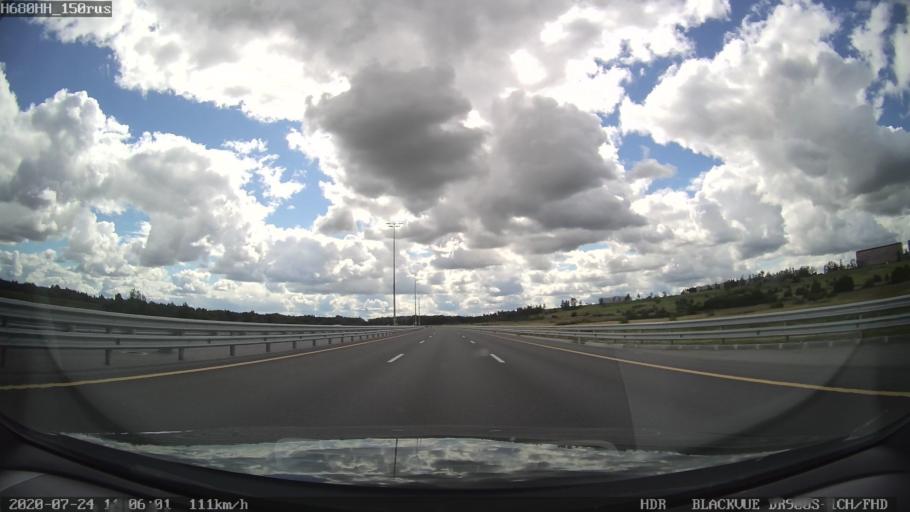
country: RU
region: St.-Petersburg
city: Shushary
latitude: 59.7691
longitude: 30.3658
